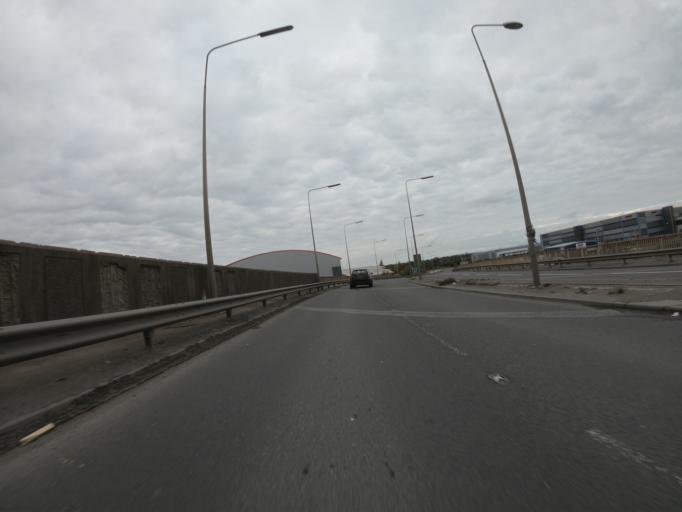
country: GB
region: England
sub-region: Borough of Thurrock
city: Tilbury
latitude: 51.4657
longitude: 0.3477
